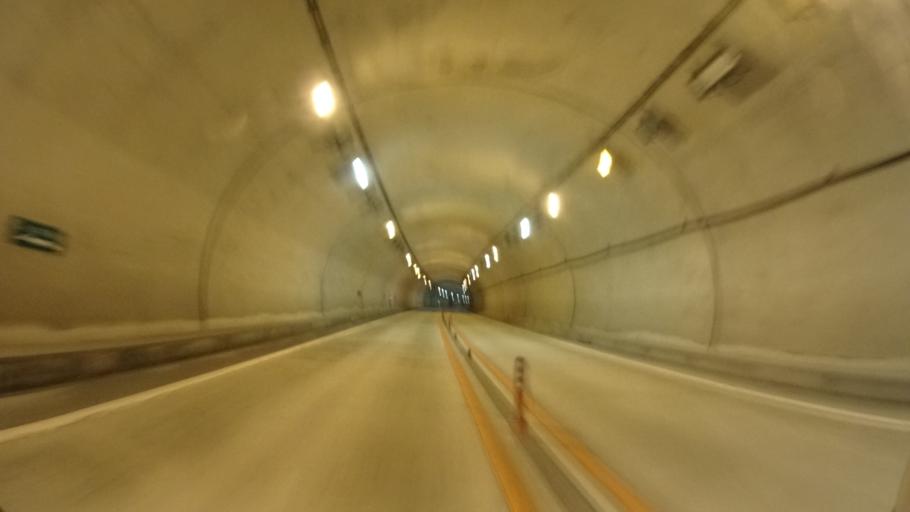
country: JP
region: Hyogo
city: Yamazakicho-nakabirose
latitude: 35.1072
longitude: 134.3303
